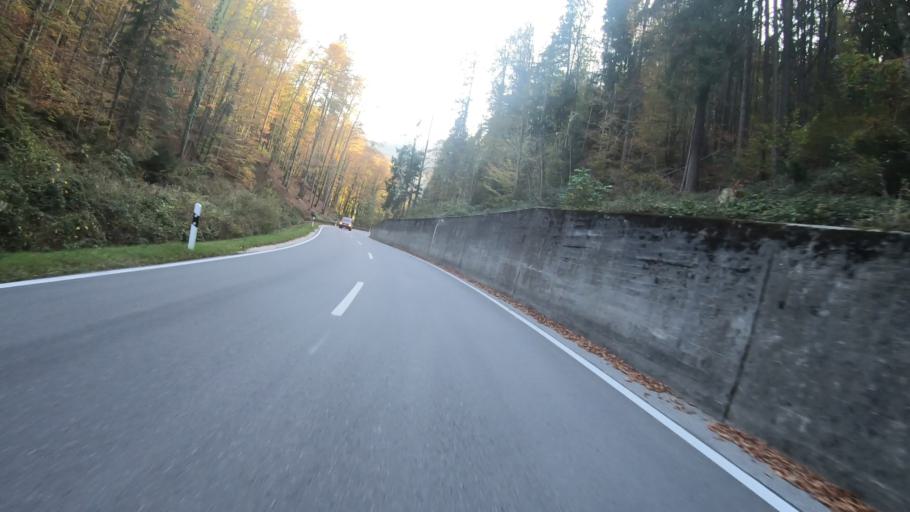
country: DE
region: Bavaria
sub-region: Upper Bavaria
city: Bergen
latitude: 47.8103
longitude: 12.6139
